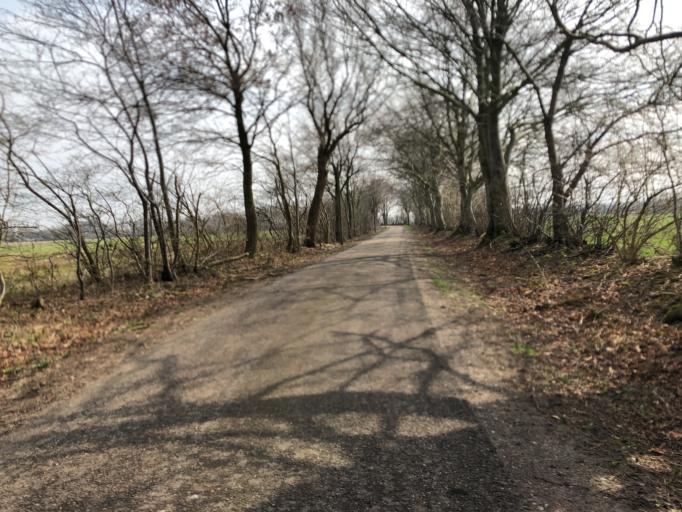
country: DE
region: Schleswig-Holstein
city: Wanderup
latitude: 54.6878
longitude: 9.3070
